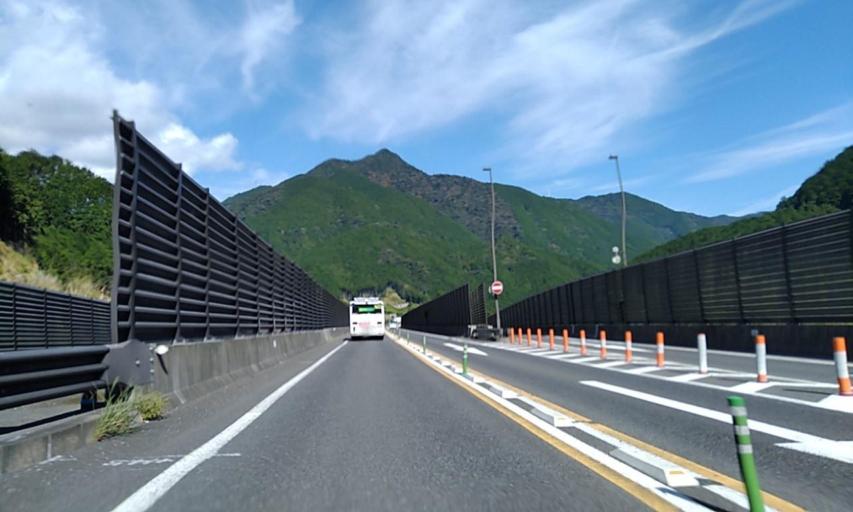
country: JP
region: Mie
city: Owase
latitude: 33.9680
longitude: 136.1617
